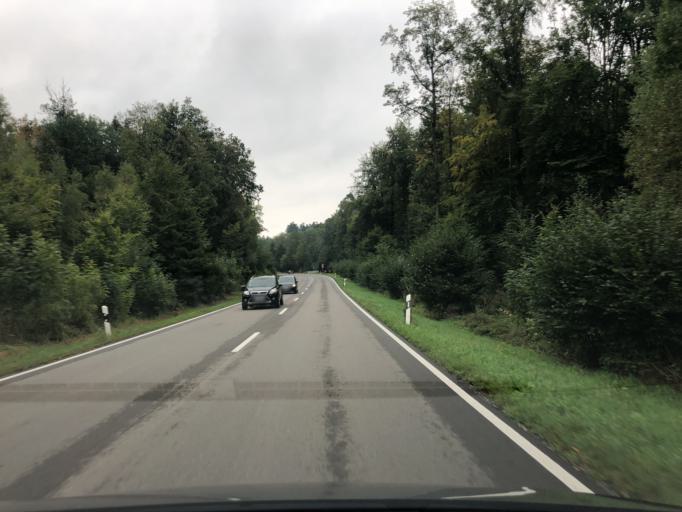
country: DE
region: Baden-Wuerttemberg
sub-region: Regierungsbezirk Stuttgart
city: Gerlingen
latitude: 48.7491
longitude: 9.0543
